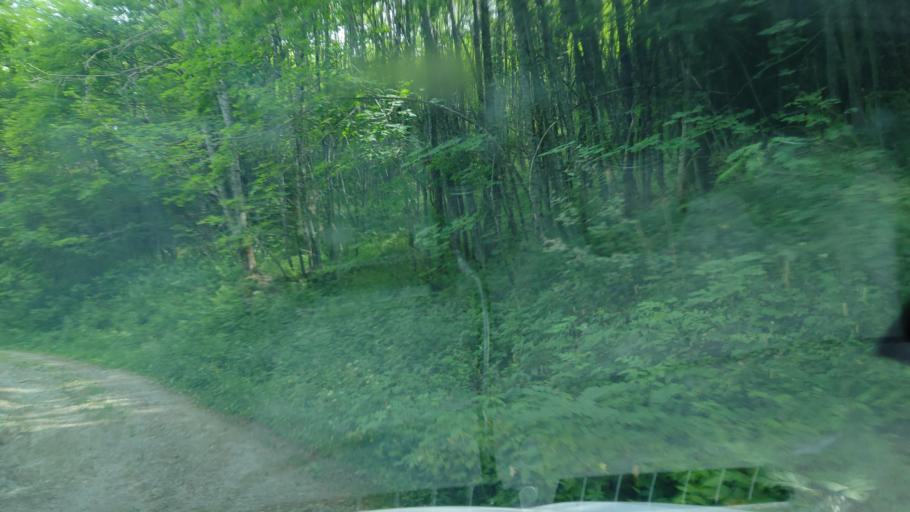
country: FR
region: Rhone-Alpes
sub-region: Departement de la Savoie
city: Cruet
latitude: 45.5935
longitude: 6.1059
